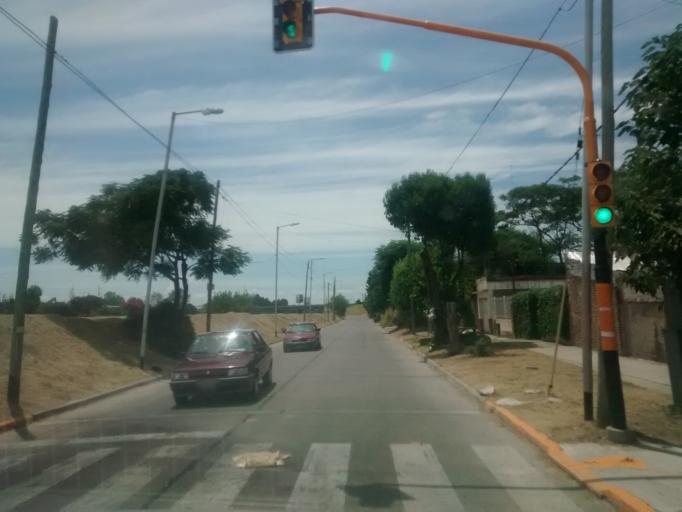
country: AR
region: Buenos Aires
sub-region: Partido de Avellaneda
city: Avellaneda
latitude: -34.6869
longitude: -58.3220
